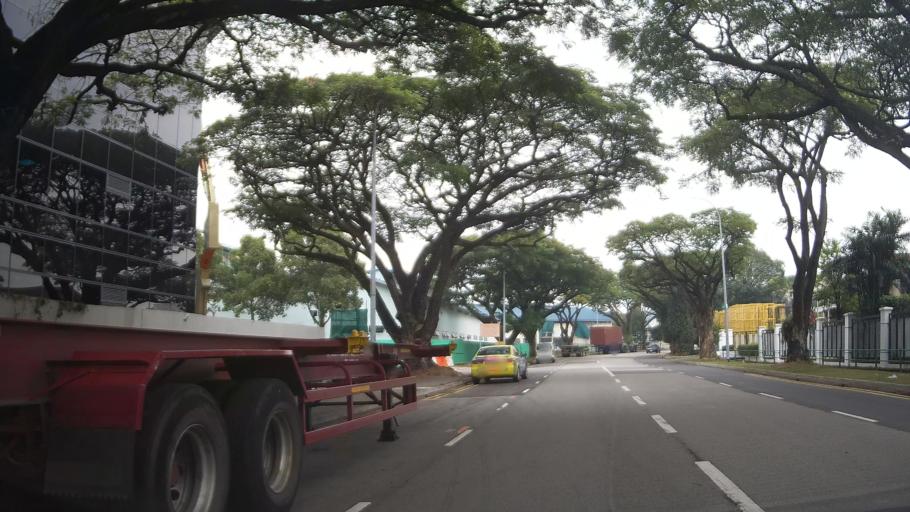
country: MY
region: Johor
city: Johor Bahru
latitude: 1.3158
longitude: 103.6640
